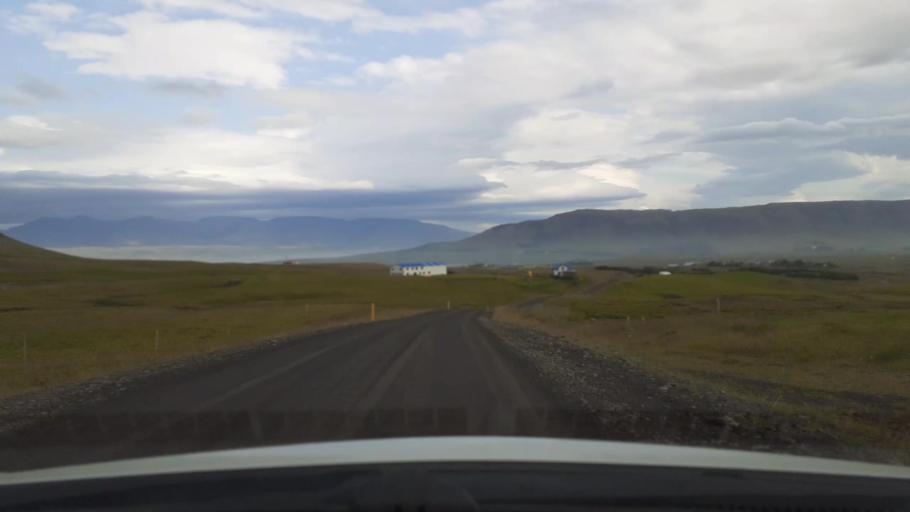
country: IS
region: Capital Region
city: Mosfellsbaer
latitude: 64.3078
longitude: -21.6558
